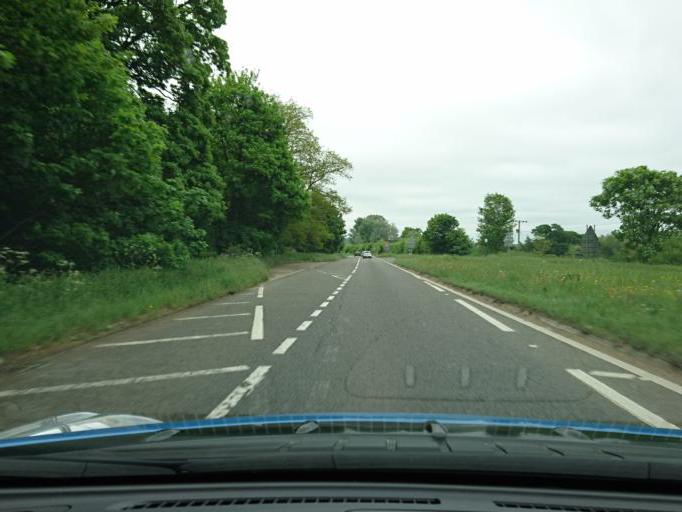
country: GB
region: England
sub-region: Oxfordshire
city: Marcham
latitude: 51.7049
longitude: -1.3441
